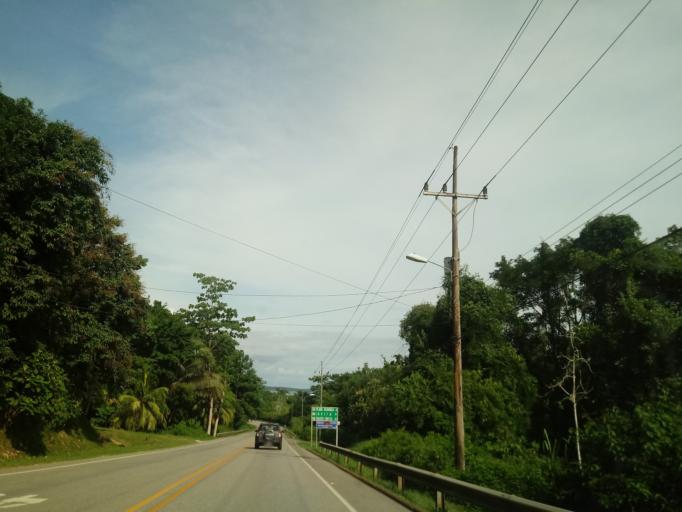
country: CR
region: San Jose
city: Daniel Flores
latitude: 9.2074
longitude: -83.8018
